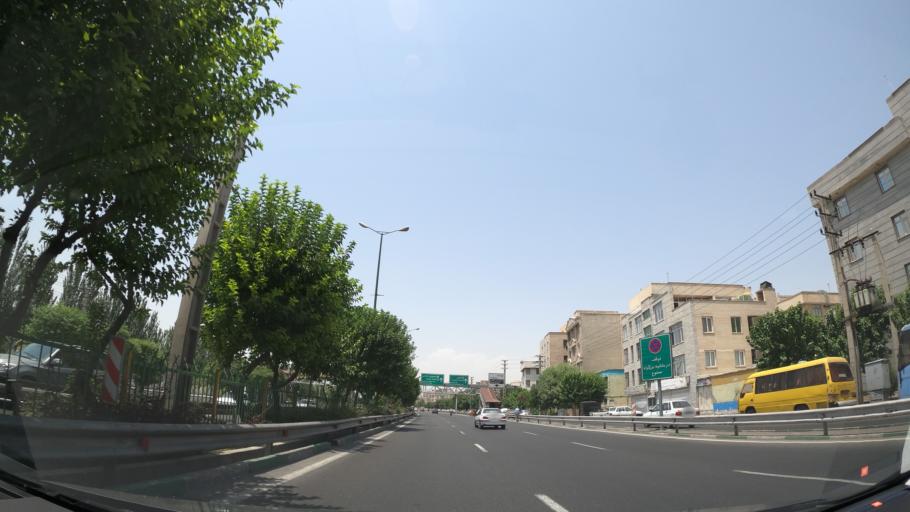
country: IR
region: Tehran
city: Tehran
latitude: 35.6483
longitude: 51.3905
